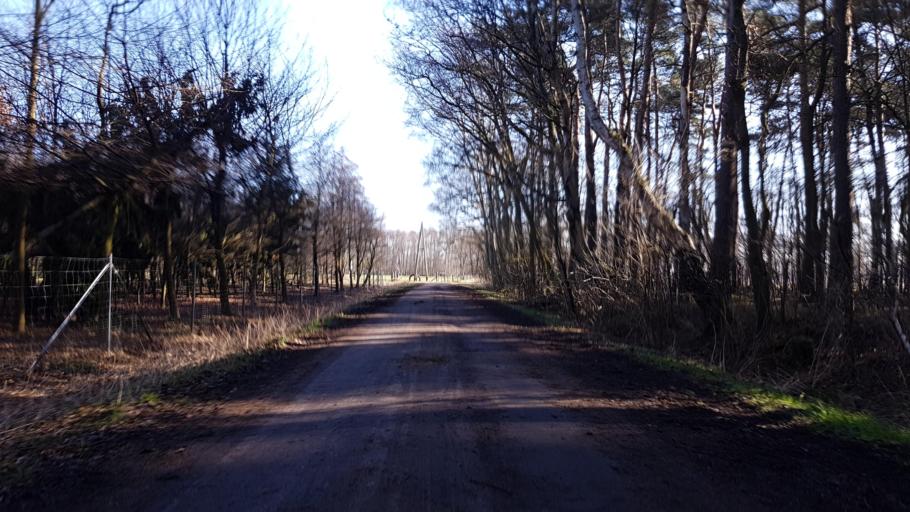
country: DE
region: Lower Saxony
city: Garbsen-Mitte
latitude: 52.4549
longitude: 9.6343
